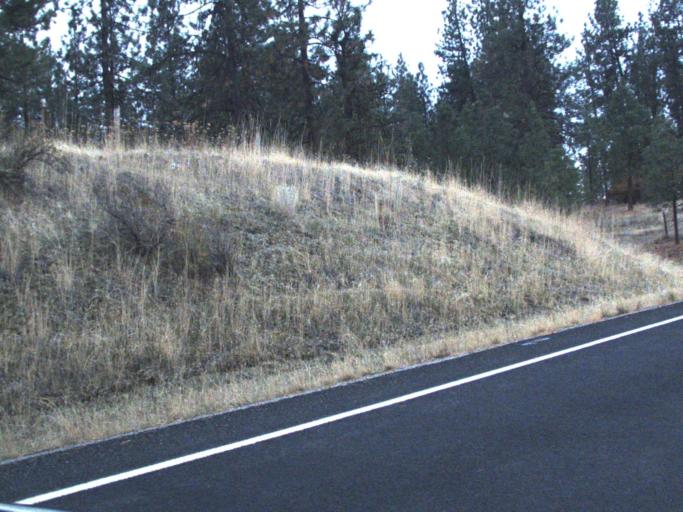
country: US
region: Washington
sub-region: Lincoln County
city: Davenport
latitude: 47.9145
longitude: -118.3320
